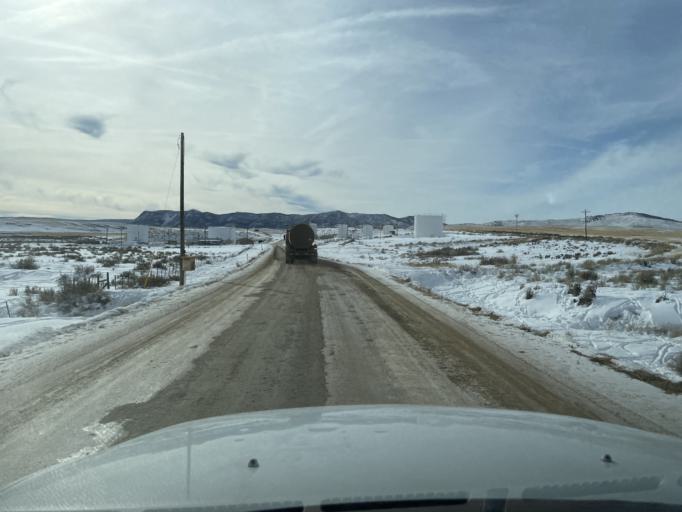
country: US
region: Colorado
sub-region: Moffat County
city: Craig
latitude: 40.3144
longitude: -107.6926
